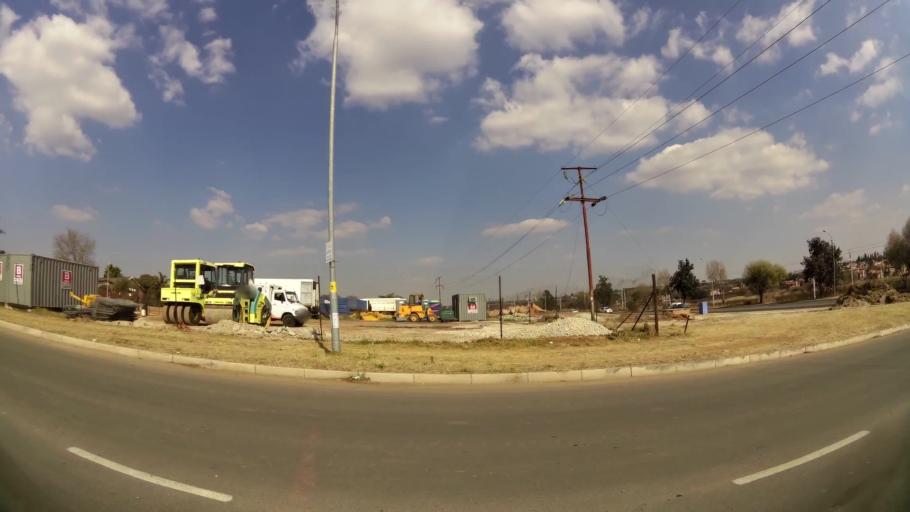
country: ZA
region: Gauteng
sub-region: City of Johannesburg Metropolitan Municipality
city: Modderfontein
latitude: -26.0828
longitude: 28.2243
